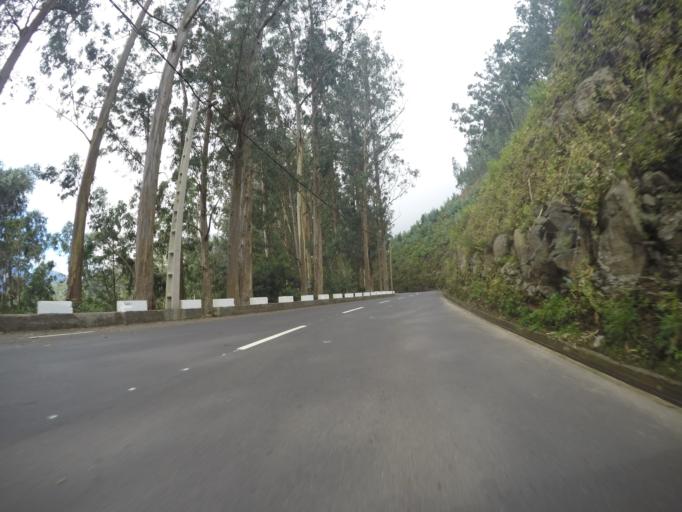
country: PT
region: Madeira
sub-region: Camara de Lobos
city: Curral das Freiras
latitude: 32.6958
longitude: -16.9544
